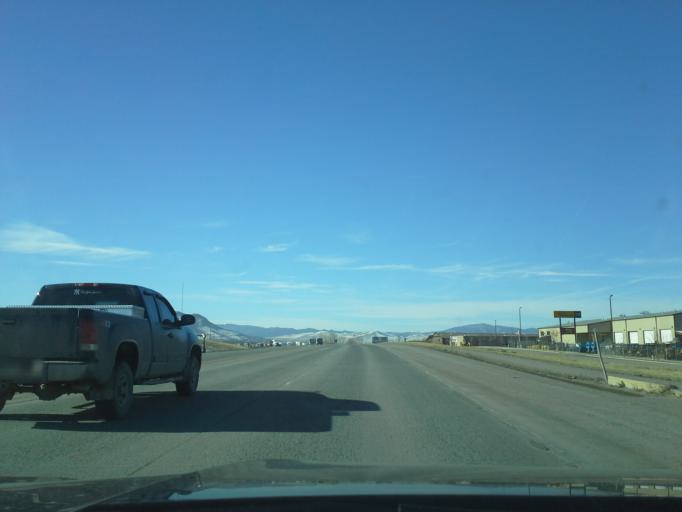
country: US
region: Montana
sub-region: Lewis and Clark County
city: East Helena
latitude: 46.5911
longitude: -111.9572
